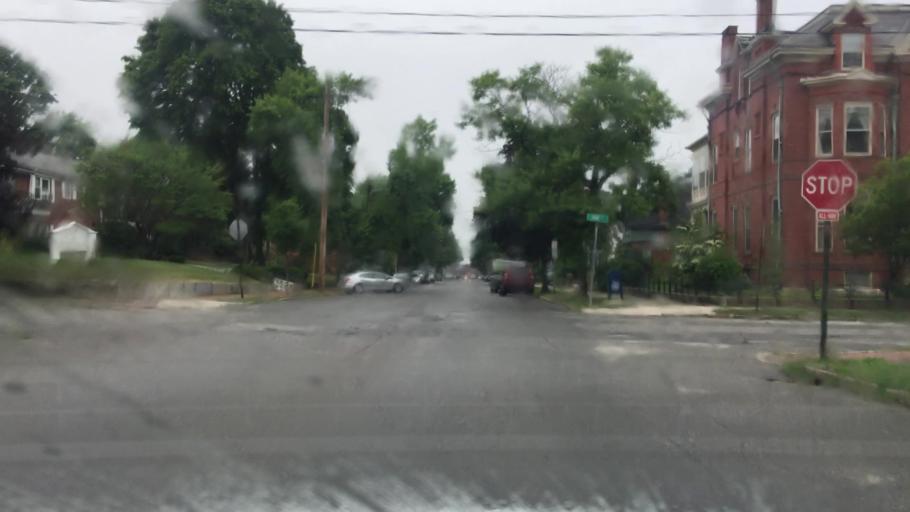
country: US
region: Maine
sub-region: Cumberland County
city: Portland
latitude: 43.6494
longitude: -70.2733
